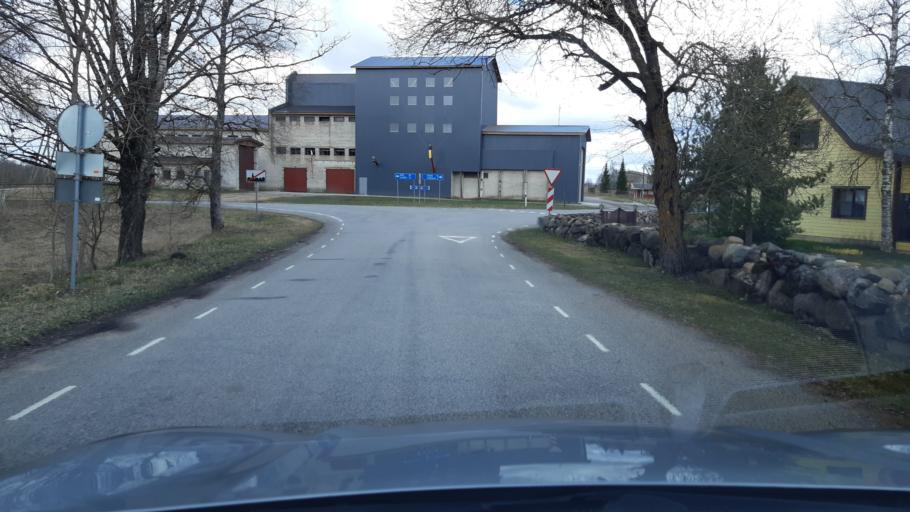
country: EE
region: Raplamaa
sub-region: Kehtna vald
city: Kehtna
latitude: 59.0452
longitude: 25.1164
